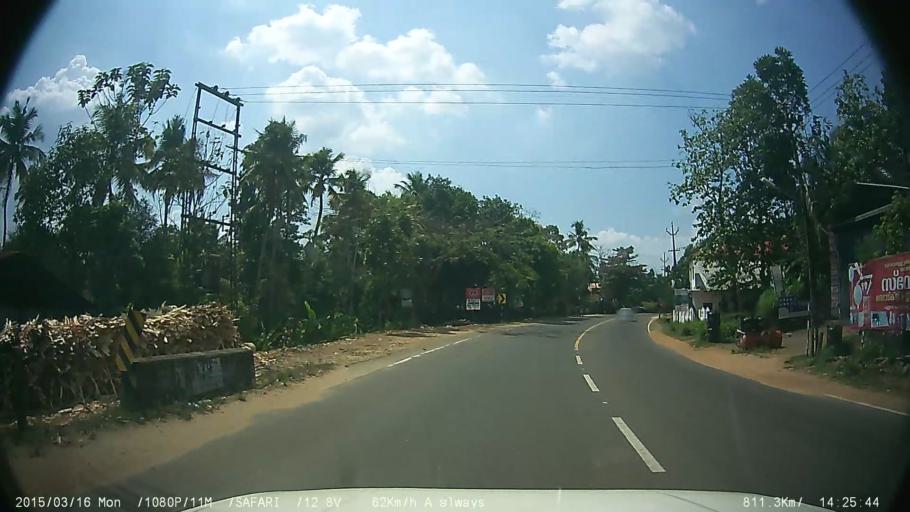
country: IN
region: Kerala
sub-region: Ernakulam
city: Perumbavoor
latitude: 10.0863
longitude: 76.5015
